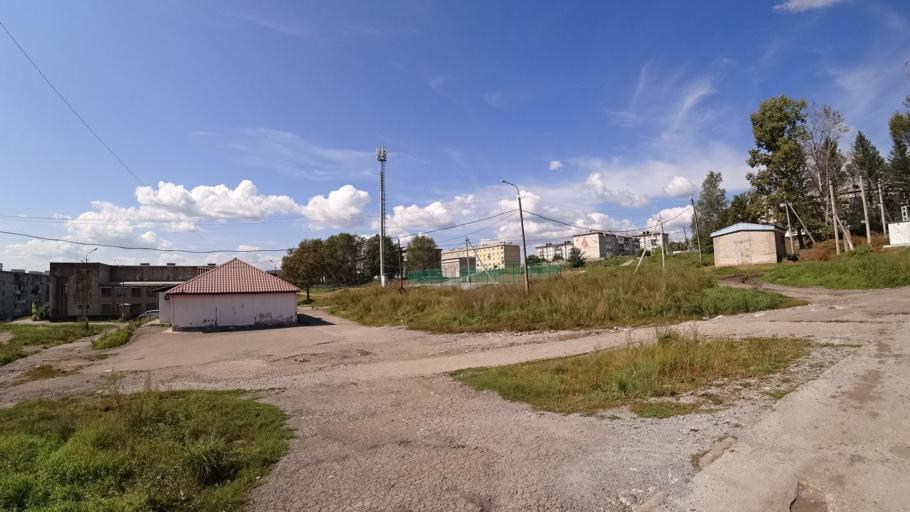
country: RU
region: Jewish Autonomous Oblast
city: Londoko
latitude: 49.0140
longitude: 131.8860
